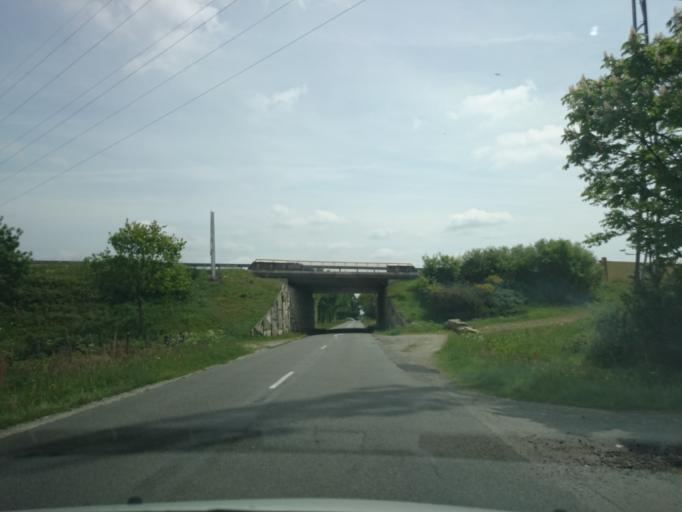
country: FR
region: Pays de la Loire
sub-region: Departement de la Loire-Atlantique
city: La Montagne
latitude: 47.1704
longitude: -1.6769
